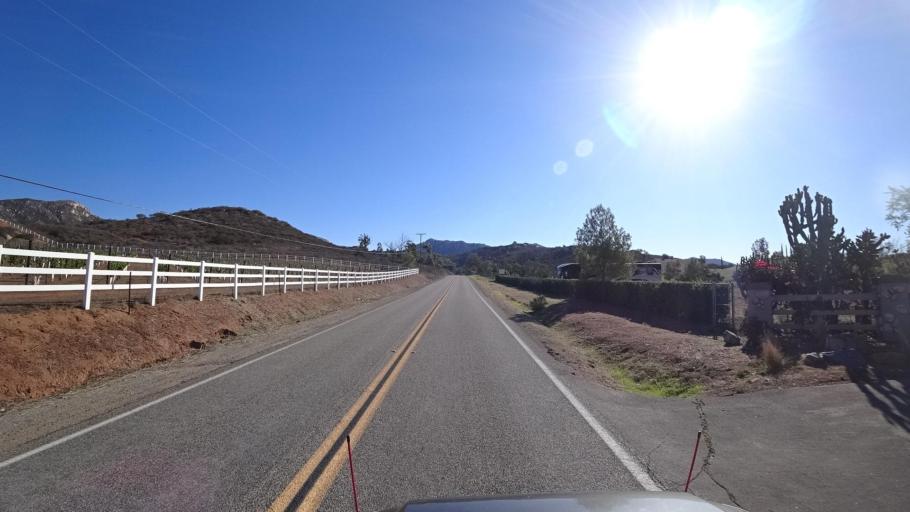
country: US
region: California
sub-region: San Diego County
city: Jamul
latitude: 32.6654
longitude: -116.7935
